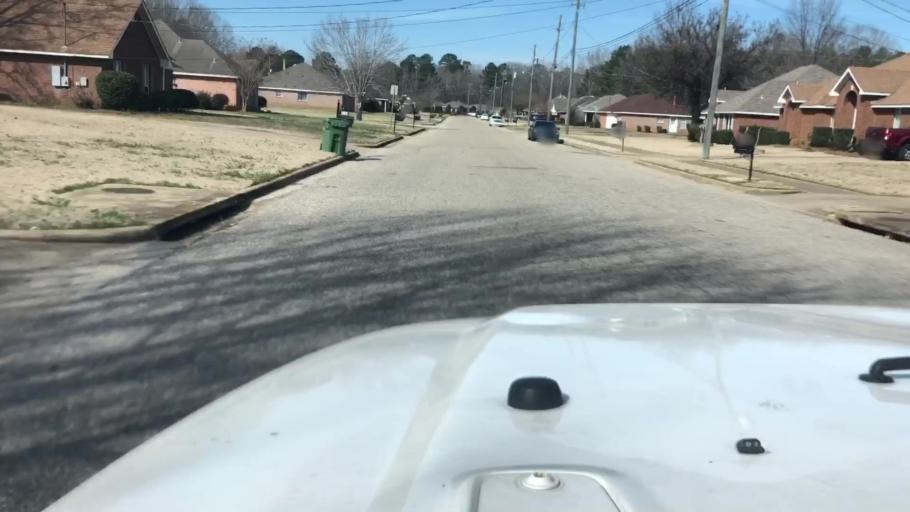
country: US
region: Alabama
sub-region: Elmore County
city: Blue Ridge
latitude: 32.4092
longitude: -86.1955
